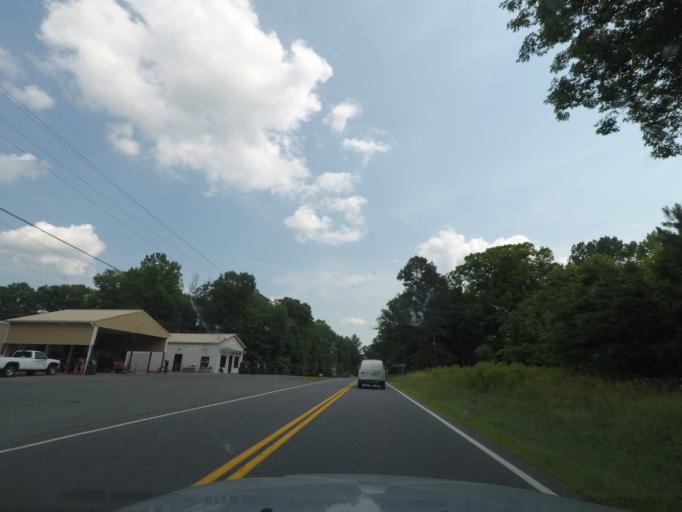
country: US
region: Virginia
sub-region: Fluvanna County
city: Palmyra
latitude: 37.9042
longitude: -78.2569
